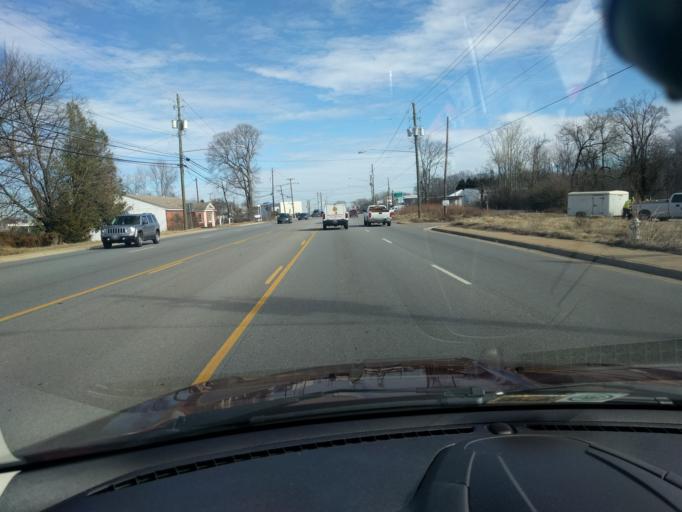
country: US
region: Virginia
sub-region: City of Lynchburg
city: West Lynchburg
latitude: 37.3964
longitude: -79.2271
